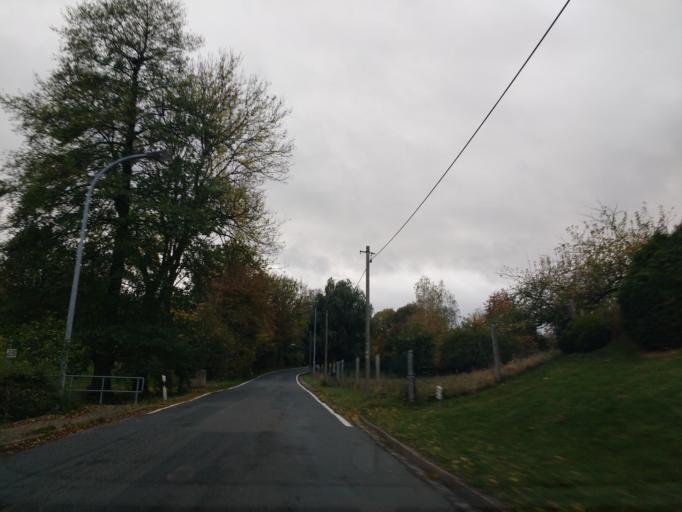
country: DE
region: Thuringia
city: Grossbodungen
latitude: 51.5113
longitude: 10.5137
